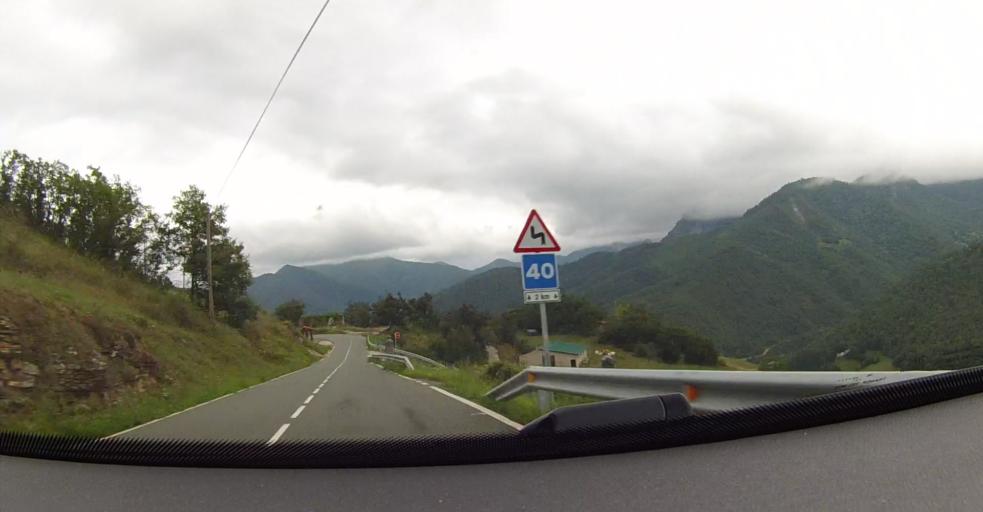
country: ES
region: Cantabria
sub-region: Provincia de Cantabria
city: Camaleno
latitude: 43.0947
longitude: -4.6877
